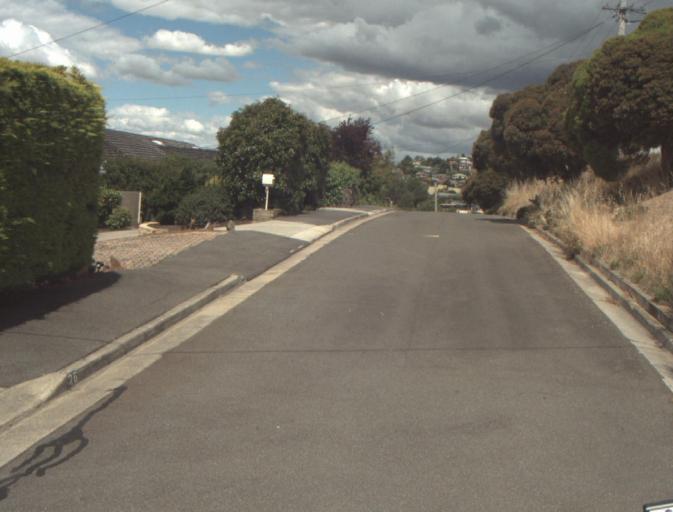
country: AU
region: Tasmania
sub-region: Launceston
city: Launceston
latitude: -41.4316
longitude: 147.1149
